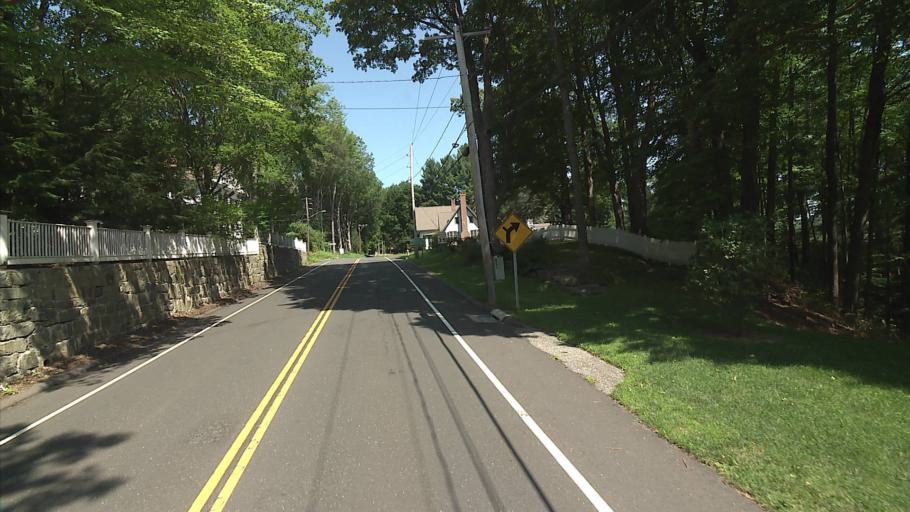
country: US
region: Connecticut
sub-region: Litchfield County
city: Winchester Center
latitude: 41.9956
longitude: -73.2027
